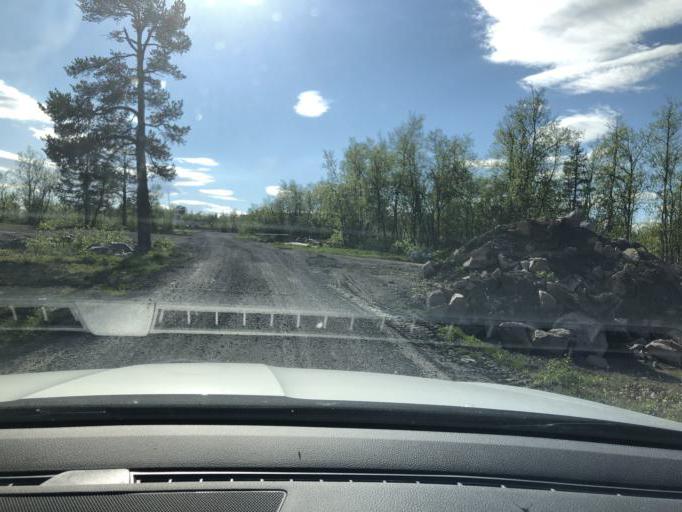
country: SE
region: Norrbotten
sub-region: Kiruna Kommun
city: Kiruna
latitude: 67.8538
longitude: 20.2773
